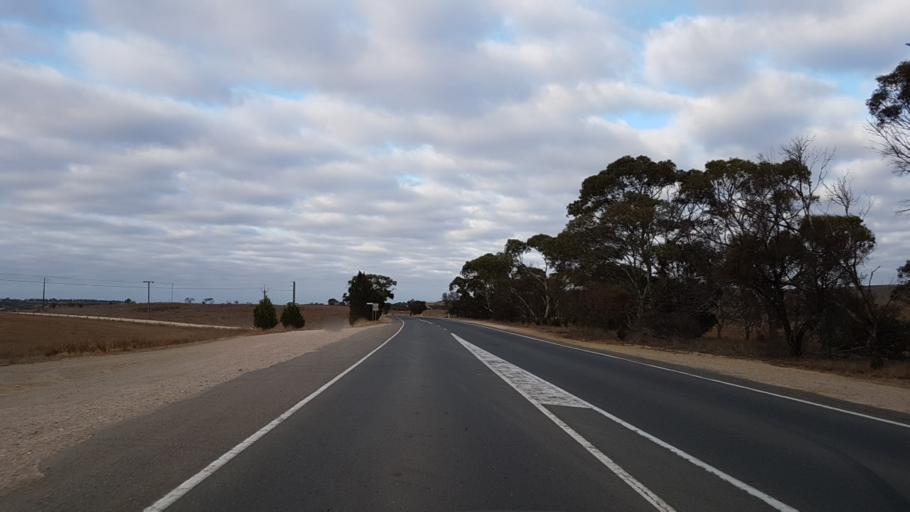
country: AU
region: South Australia
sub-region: Mount Barker
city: Callington
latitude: -35.1305
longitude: 139.0346
